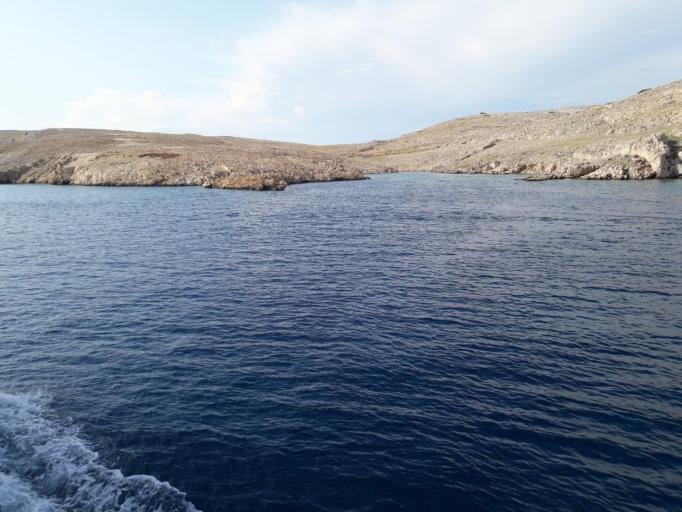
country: HR
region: Primorsko-Goranska
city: Banjol
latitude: 44.7051
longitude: 14.8650
